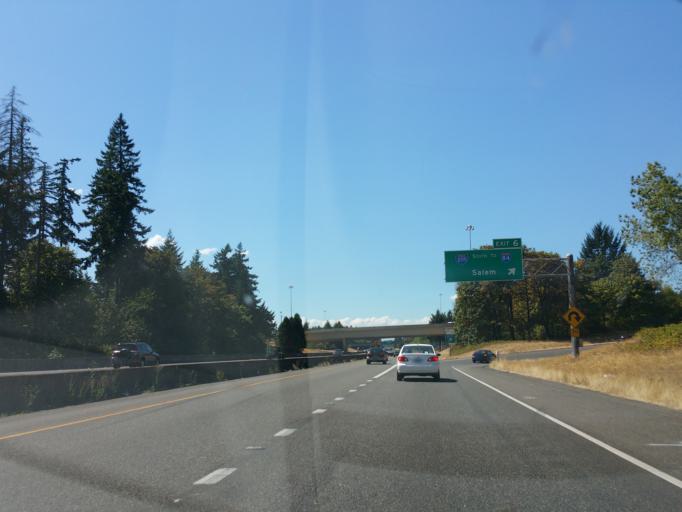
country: US
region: Washington
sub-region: Clark County
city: Orchards
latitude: 45.6039
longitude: -122.5513
